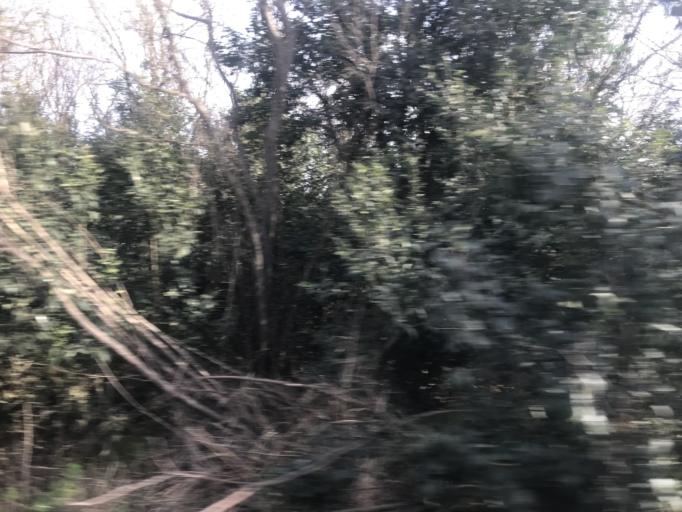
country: AR
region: Cordoba
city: Laguna Larga
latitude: -31.7911
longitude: -63.7908
